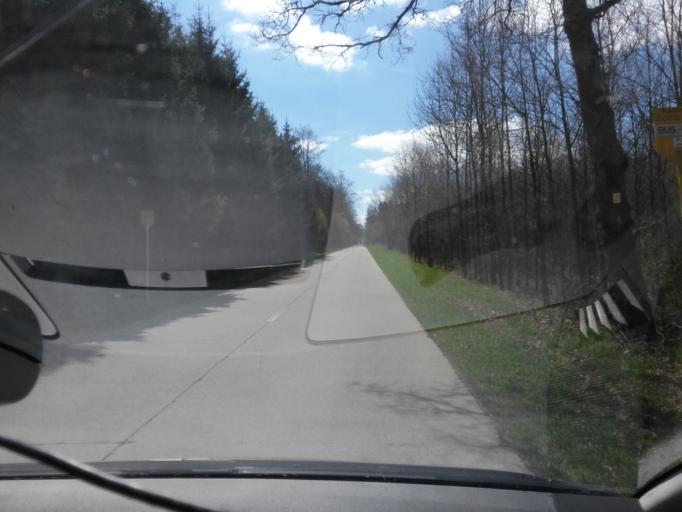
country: BE
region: Wallonia
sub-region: Province du Luxembourg
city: Libin
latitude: 50.0048
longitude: 5.2583
